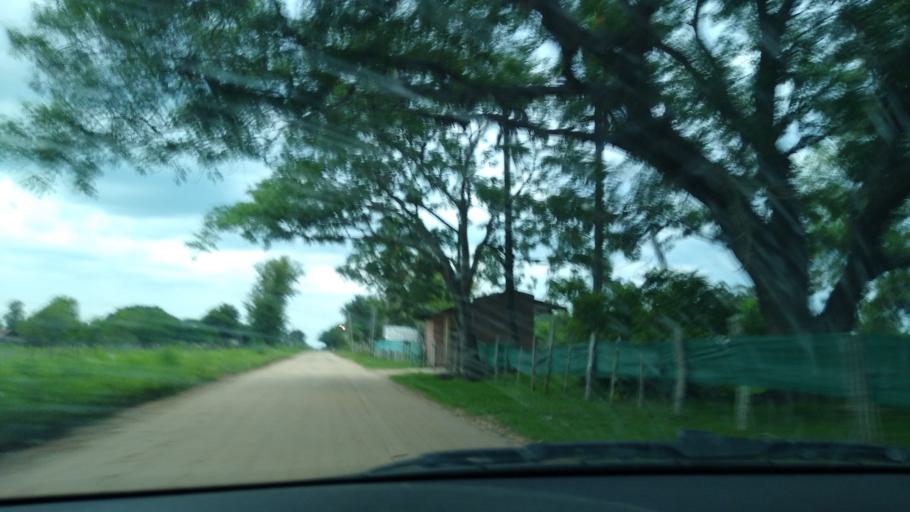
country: AR
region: Chaco
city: Puerto Vilelas
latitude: -27.5125
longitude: -58.9693
